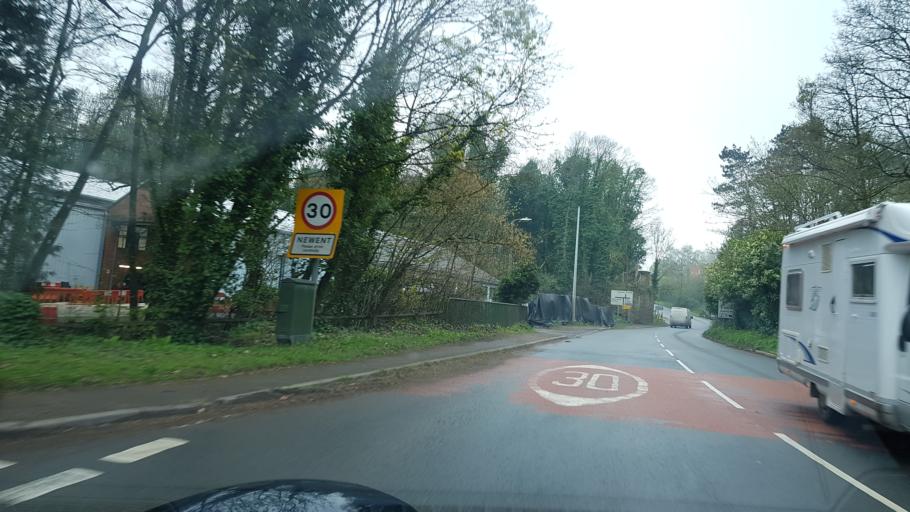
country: GB
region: England
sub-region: Gloucestershire
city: Newent
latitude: 51.9356
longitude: -2.4070
